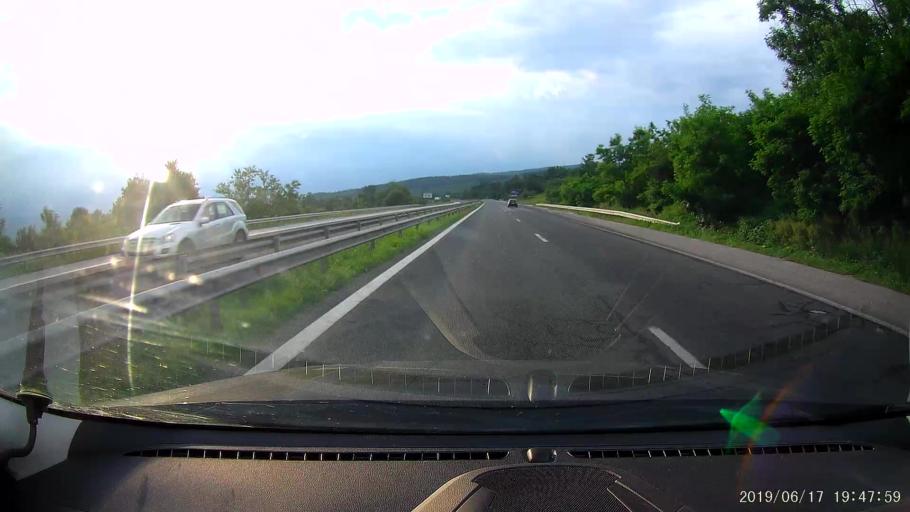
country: BG
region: Sofiya
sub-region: Obshtina Ikhtiman
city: Ikhtiman
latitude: 42.4603
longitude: 23.8339
